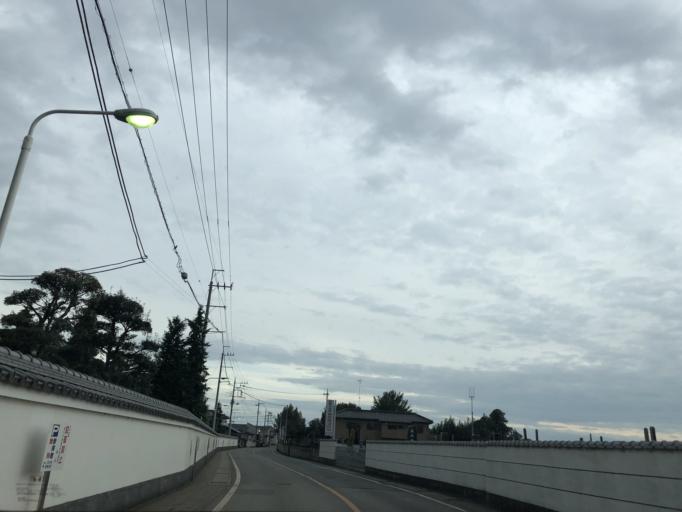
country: JP
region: Tochigi
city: Sano
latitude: 36.3113
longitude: 139.5707
